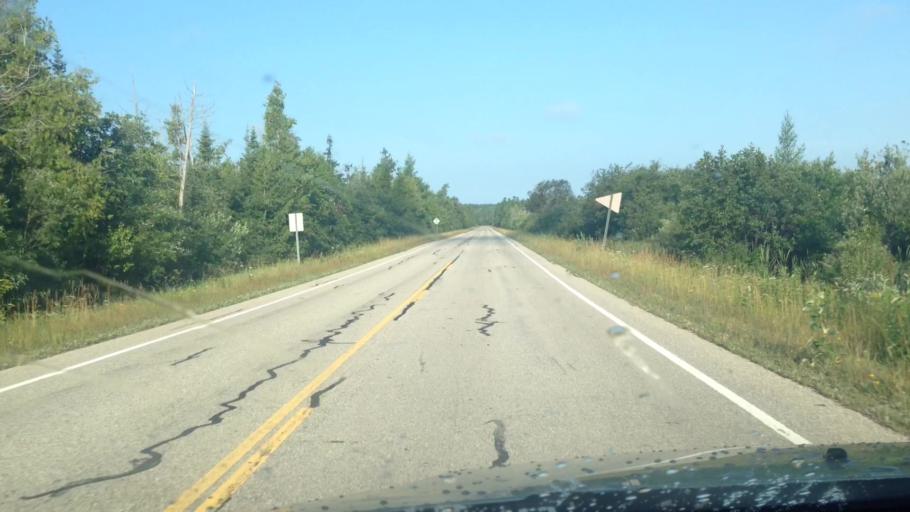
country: US
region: Michigan
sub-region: Mackinac County
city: Saint Ignace
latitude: 45.8929
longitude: -84.7710
